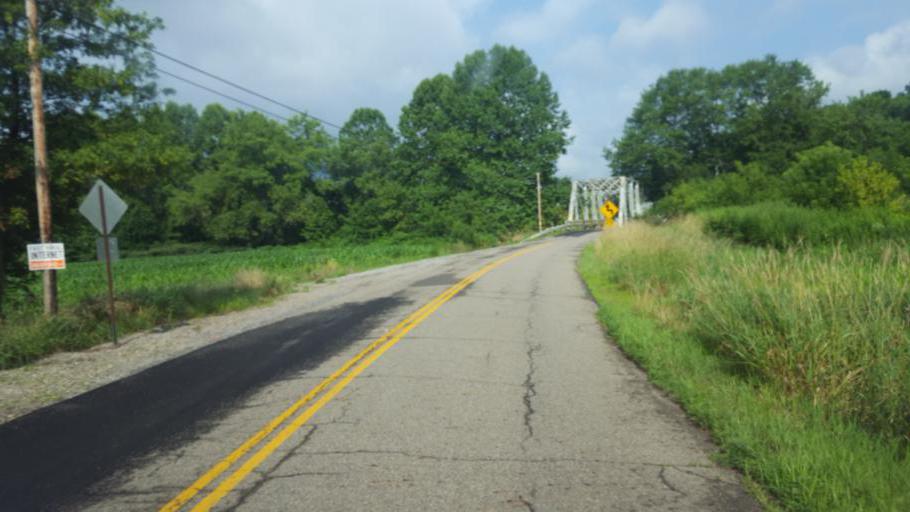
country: US
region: Ohio
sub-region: Columbiana County
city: Salineville
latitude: 40.5205
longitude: -80.8595
